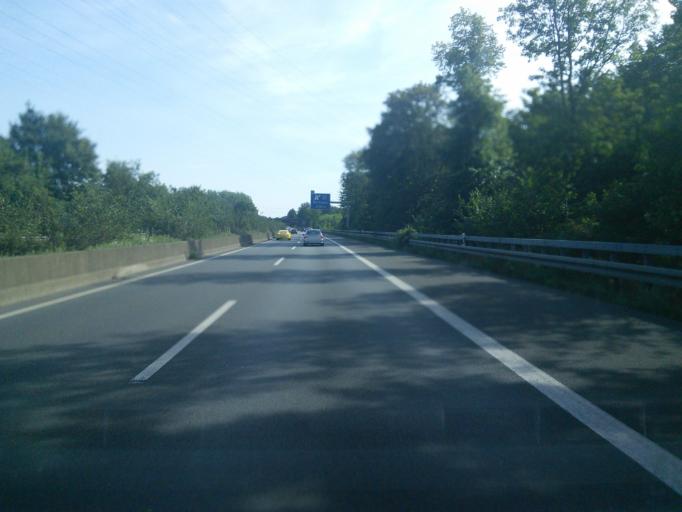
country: DE
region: North Rhine-Westphalia
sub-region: Regierungsbezirk Dusseldorf
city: Dormagen
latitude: 51.1047
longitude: 6.8001
